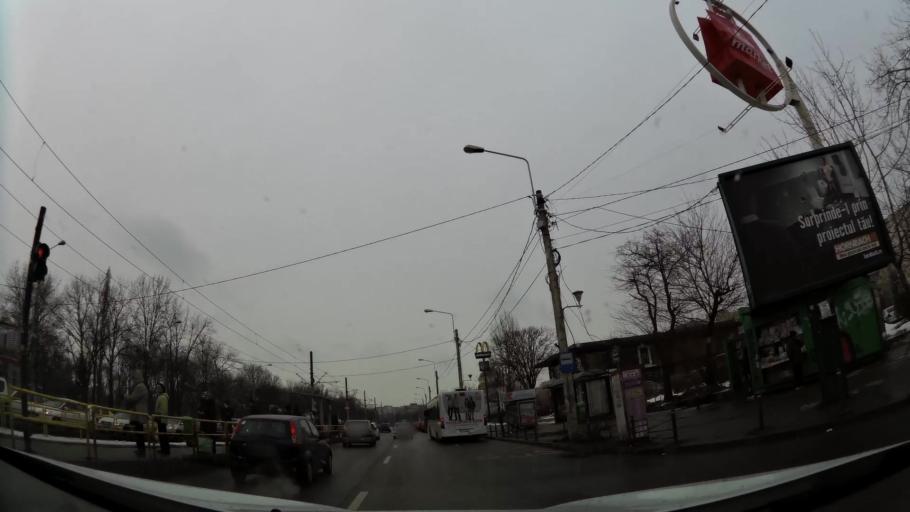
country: RO
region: Ilfov
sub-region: Comuna Chiajna
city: Rosu
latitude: 44.4180
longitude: 26.0346
